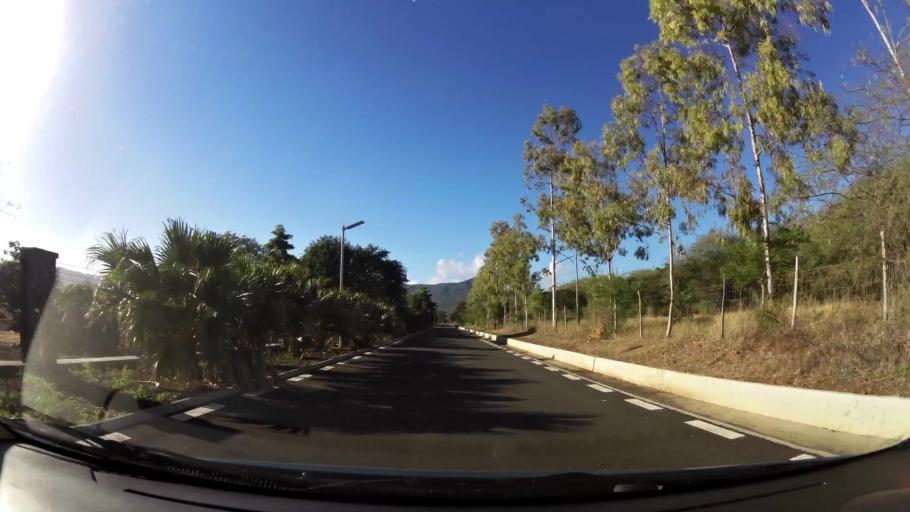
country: MU
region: Black River
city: Tamarin
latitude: -20.3419
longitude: 57.3891
